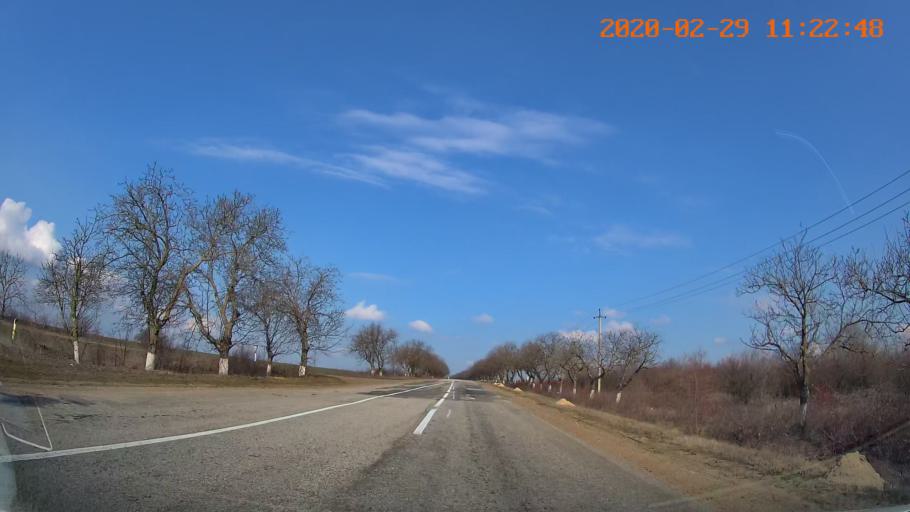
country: MD
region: Telenesti
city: Cocieri
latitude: 47.3988
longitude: 29.1610
